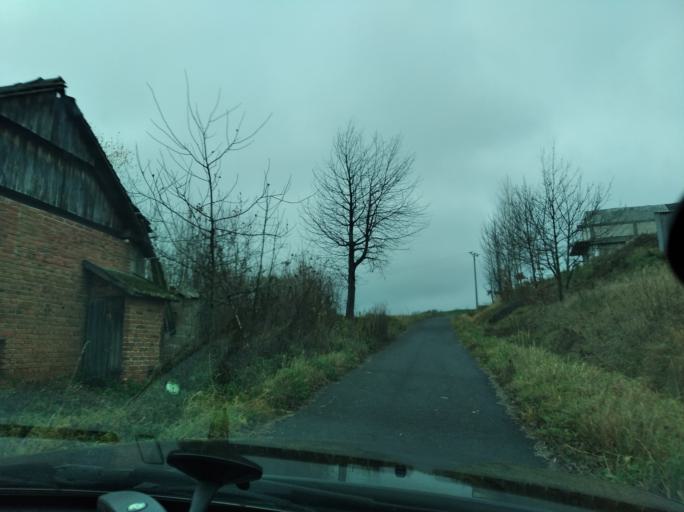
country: PL
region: Subcarpathian Voivodeship
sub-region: Powiat przeworski
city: Jawornik Polski
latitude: 49.8905
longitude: 22.2781
